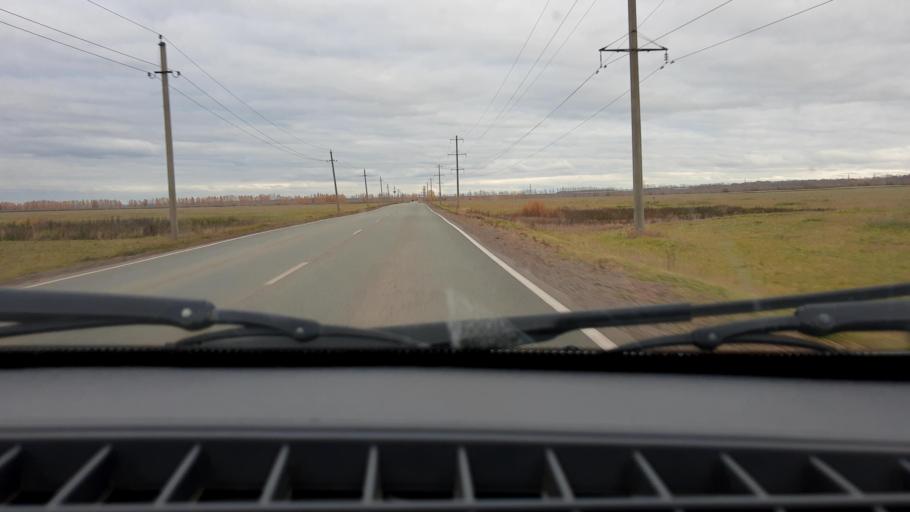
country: RU
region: Bashkortostan
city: Kabakovo
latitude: 54.5411
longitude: 56.0566
